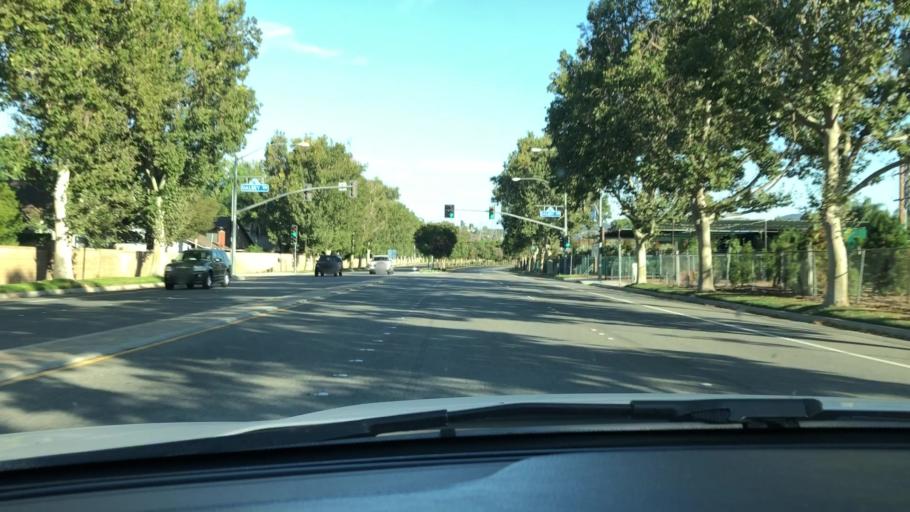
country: US
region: California
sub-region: Los Angeles County
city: Santa Clarita
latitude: 34.3855
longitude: -118.5442
